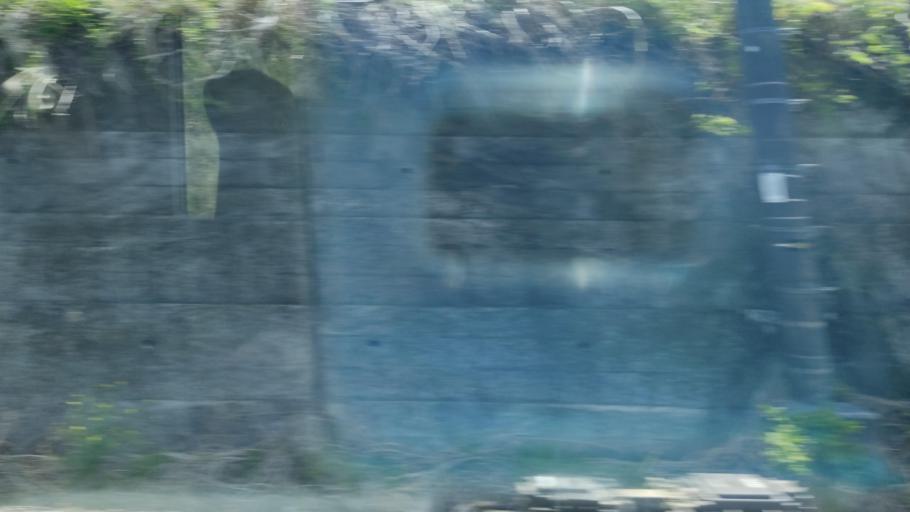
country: JP
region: Kanagawa
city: Ninomiya
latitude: 35.2942
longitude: 139.2426
